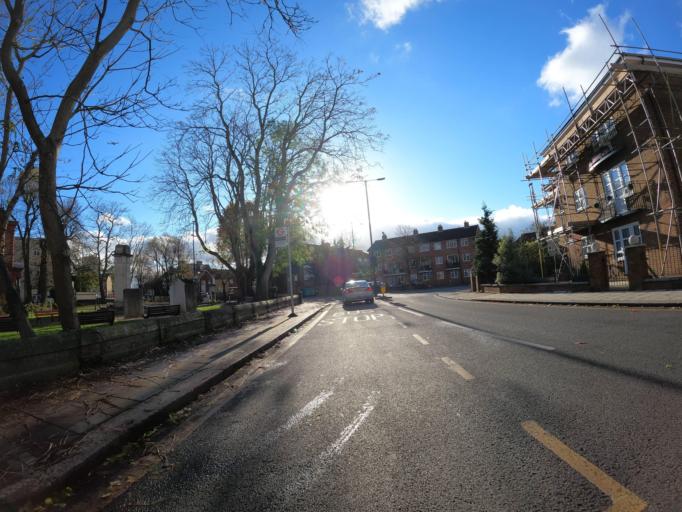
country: GB
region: England
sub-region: Greater London
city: Brentford
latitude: 51.4868
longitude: -0.3080
